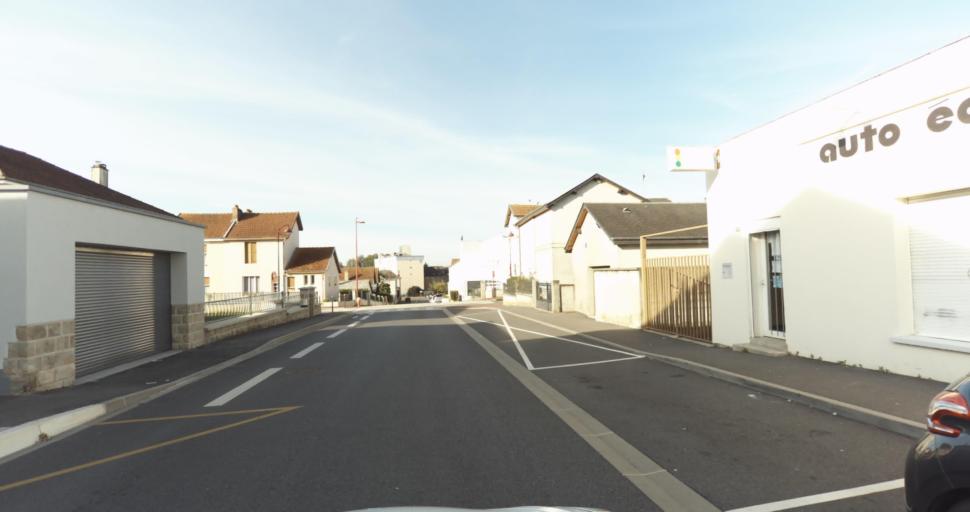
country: FR
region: Champagne-Ardenne
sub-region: Departement des Ardennes
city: Villers-Semeuse
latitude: 49.7421
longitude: 4.7459
